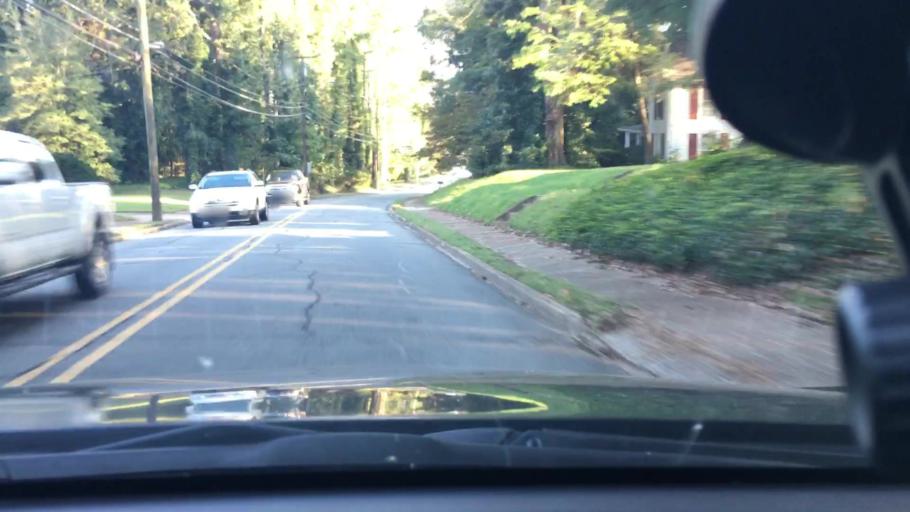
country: US
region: North Carolina
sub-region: Rutherford County
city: Rutherfordton
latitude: 35.3755
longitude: -81.9600
